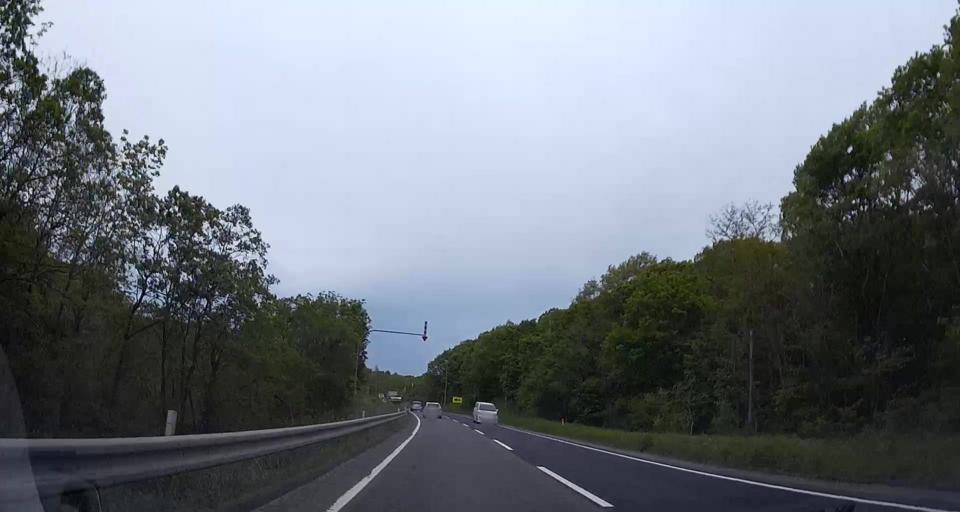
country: JP
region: Hokkaido
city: Chitose
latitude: 42.7090
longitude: 141.7459
